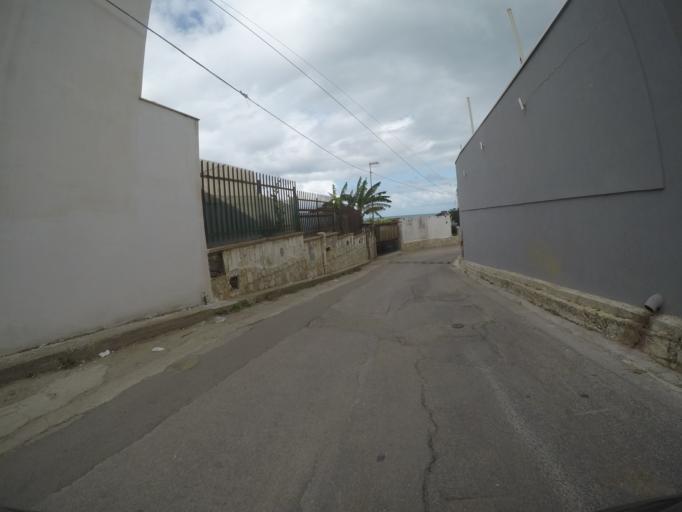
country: IT
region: Sicily
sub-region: Palermo
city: Trappeto
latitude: 38.0726
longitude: 13.0543
